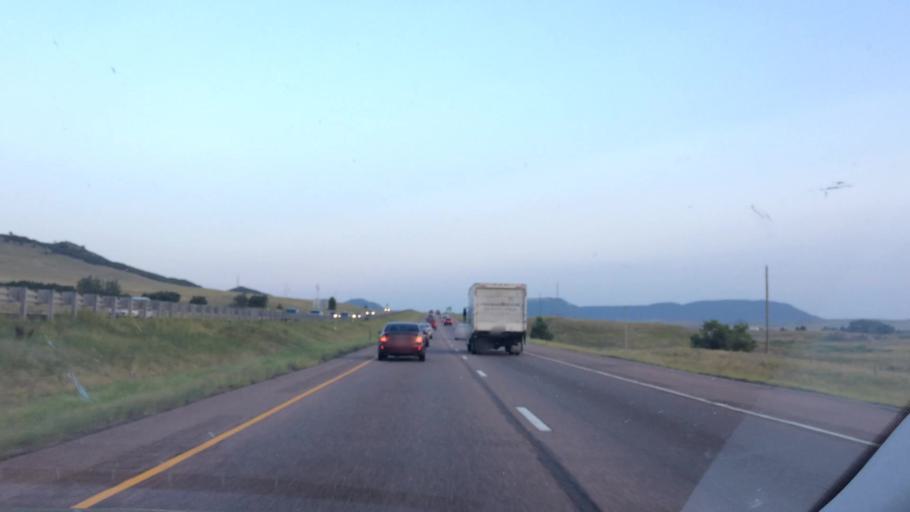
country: US
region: Colorado
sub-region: El Paso County
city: Palmer Lake
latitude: 39.2013
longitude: -104.8565
